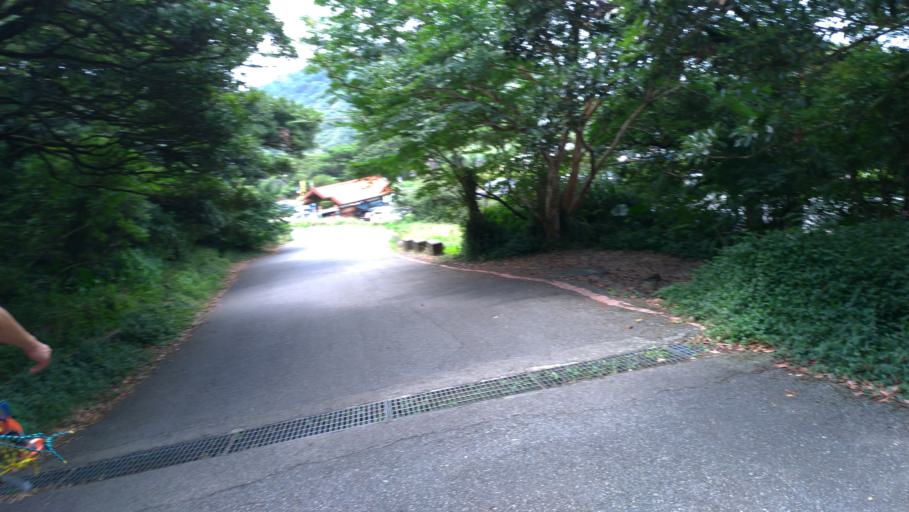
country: TW
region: Taipei
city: Taipei
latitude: 25.1856
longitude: 121.5260
